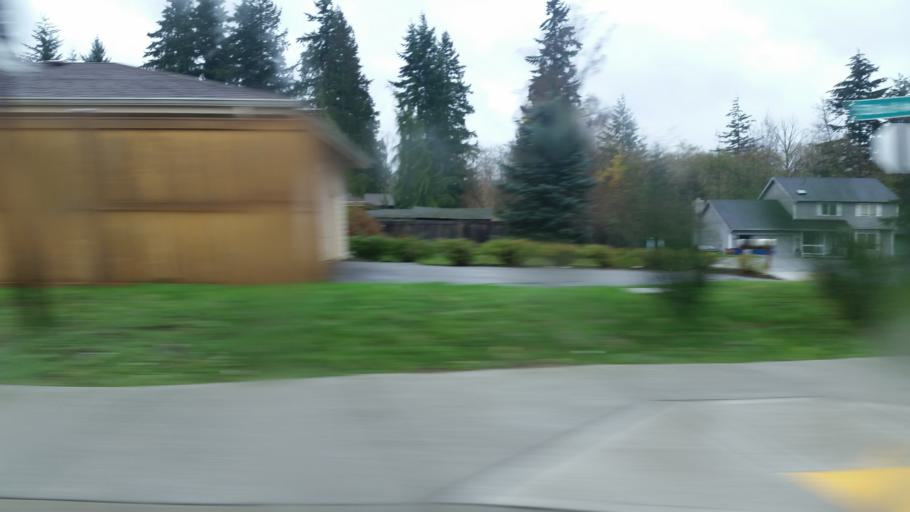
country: US
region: Washington
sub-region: Snohomish County
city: Meadowdale
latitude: 47.8539
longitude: -122.3036
